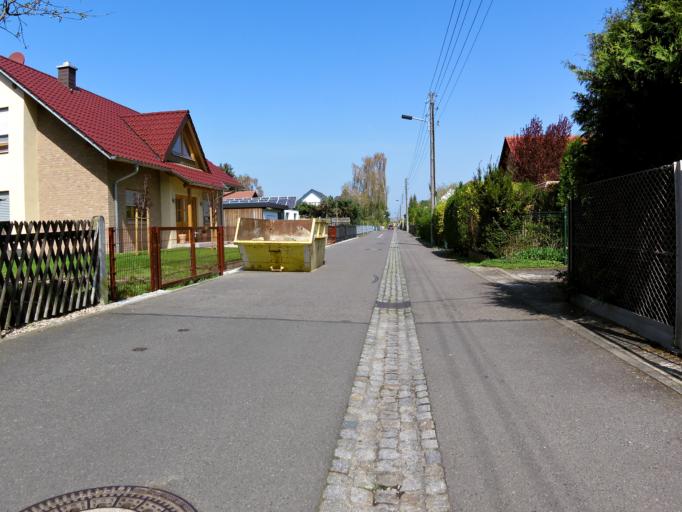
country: DE
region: Saxony
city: Leipzig
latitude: 51.3837
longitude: 12.3326
